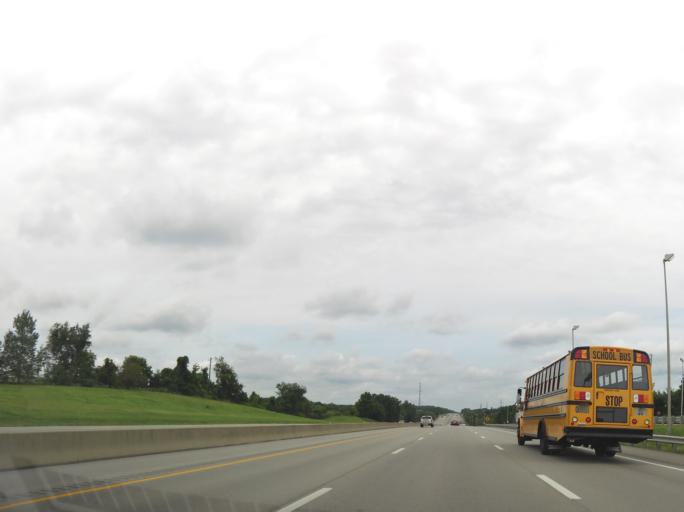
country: US
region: Kentucky
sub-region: Scott County
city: Georgetown
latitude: 38.2935
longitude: -84.5587
